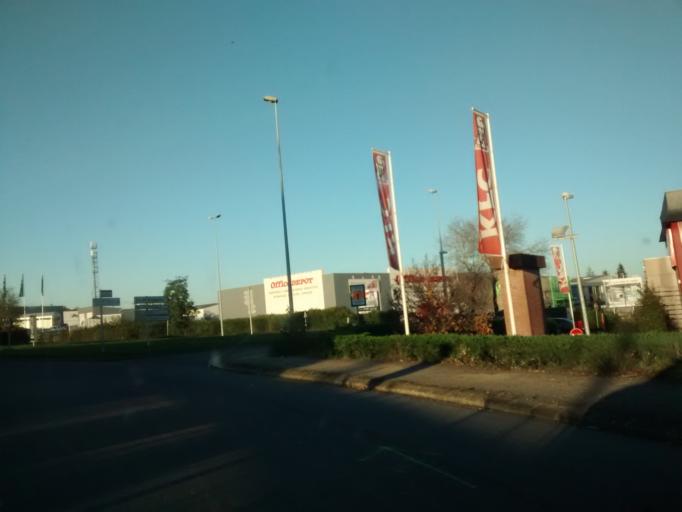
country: FR
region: Brittany
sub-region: Departement d'Ille-et-Vilaine
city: Saint-Gregoire
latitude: 48.1362
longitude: -1.6922
